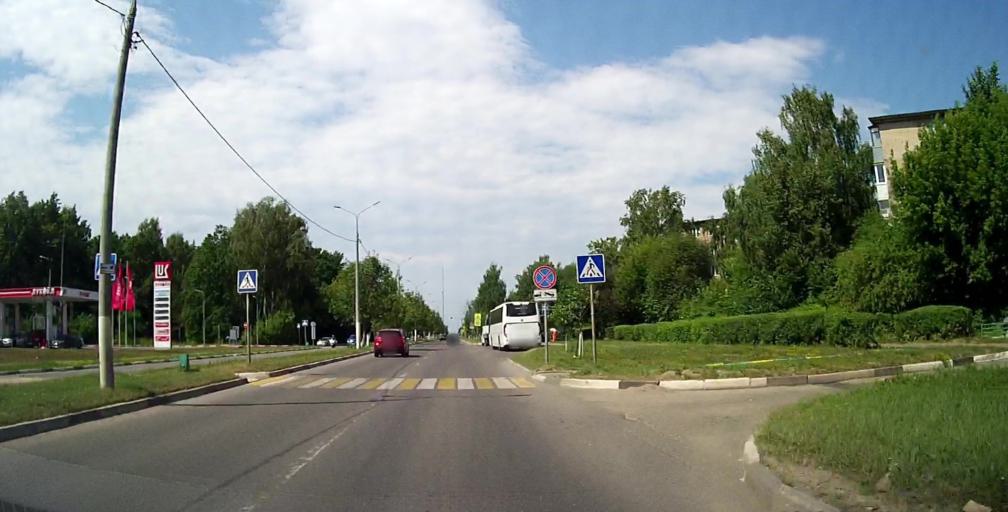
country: RU
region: Moskovskaya
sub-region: Podol'skiy Rayon
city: Podol'sk
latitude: 55.4121
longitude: 37.5231
